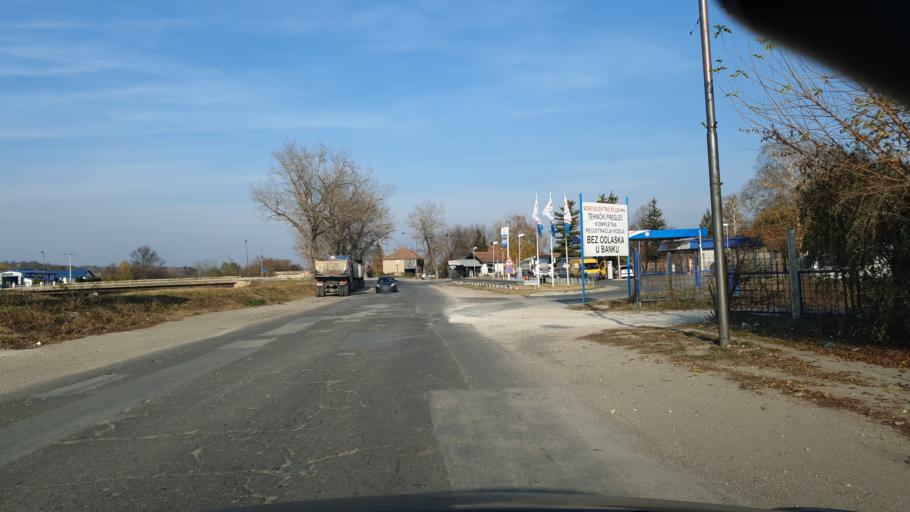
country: RS
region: Central Serbia
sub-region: Zajecarski Okrug
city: Zajecar
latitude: 43.9114
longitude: 22.2914
